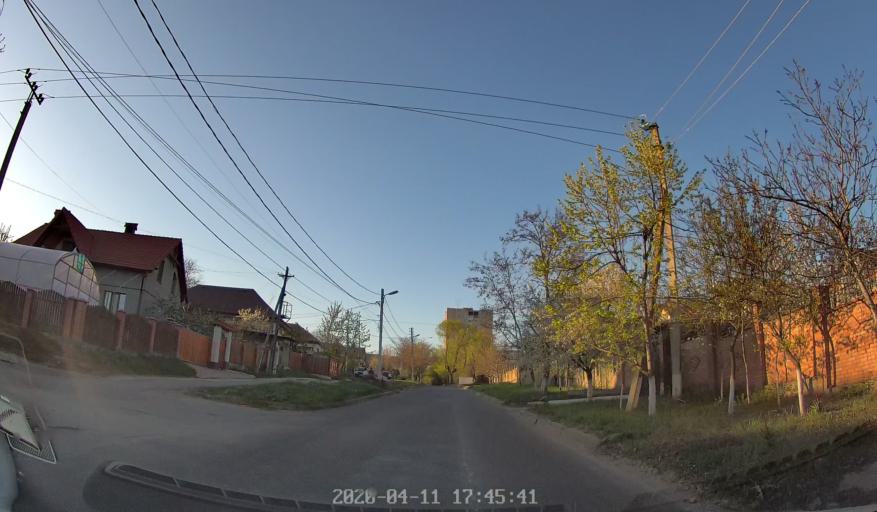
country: MD
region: Chisinau
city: Chisinau
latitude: 46.9871
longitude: 28.8222
